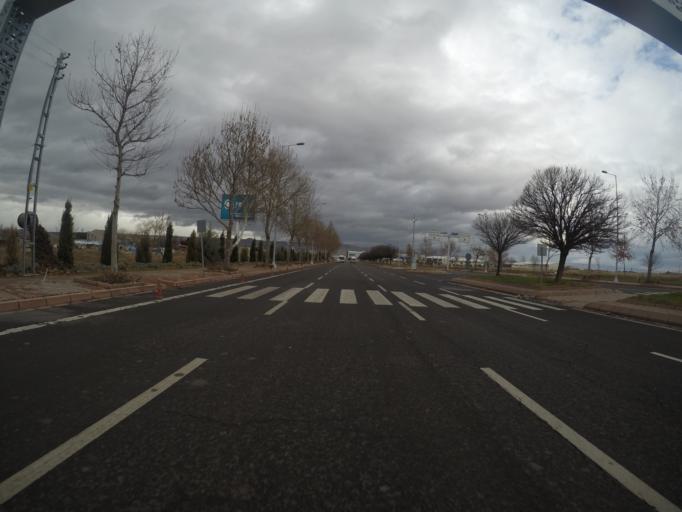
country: TR
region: Kayseri
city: Kayseri
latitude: 38.7615
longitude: 35.4819
